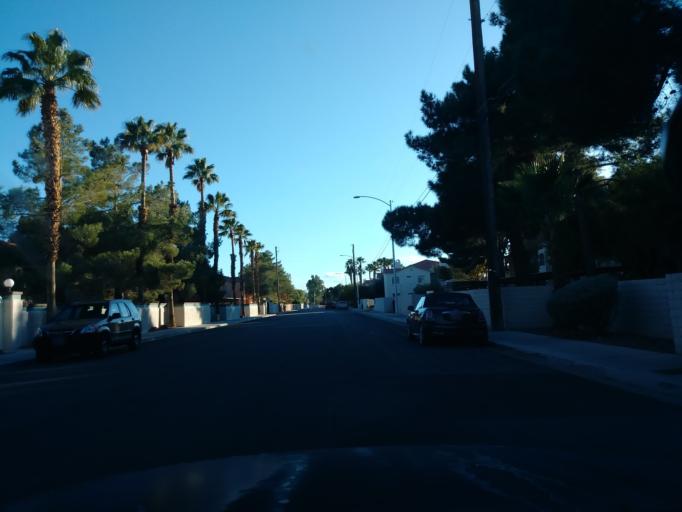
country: US
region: Nevada
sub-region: Clark County
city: Spring Valley
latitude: 36.1545
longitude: -115.2413
